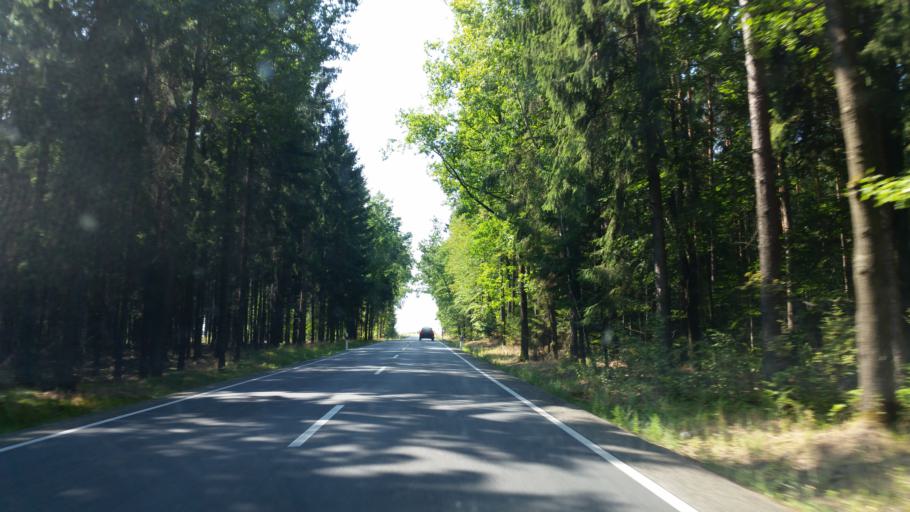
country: DE
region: Saxony
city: Grosshennersdorf
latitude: 50.9714
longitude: 14.7497
